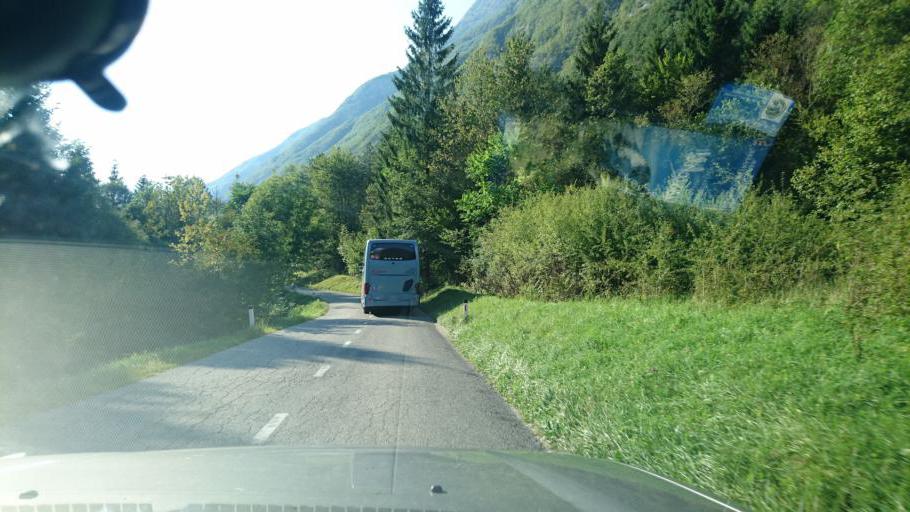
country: SI
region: Bovec
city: Bovec
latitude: 46.3366
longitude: 13.6337
